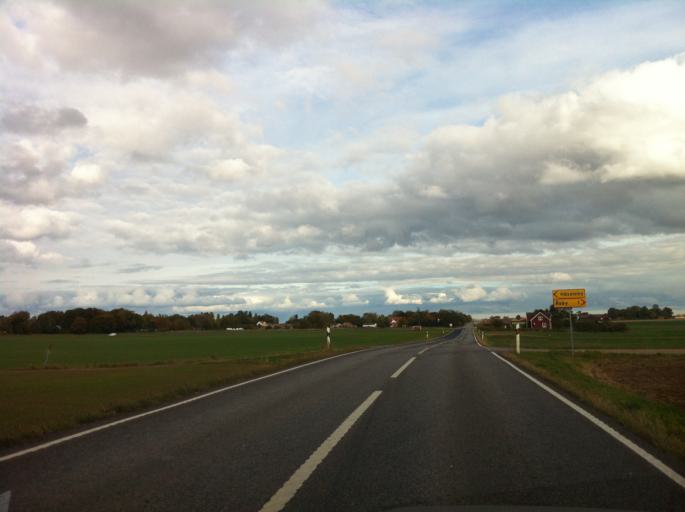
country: SE
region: OEstergoetland
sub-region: Vadstena Kommun
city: Herrestad
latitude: 58.3755
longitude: 14.7389
